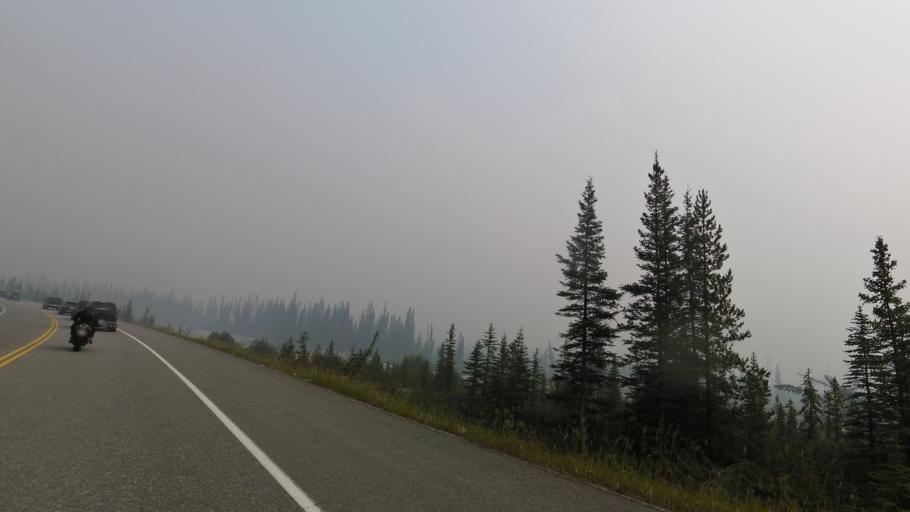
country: CA
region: Alberta
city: Banff
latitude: 50.9725
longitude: -115.9474
